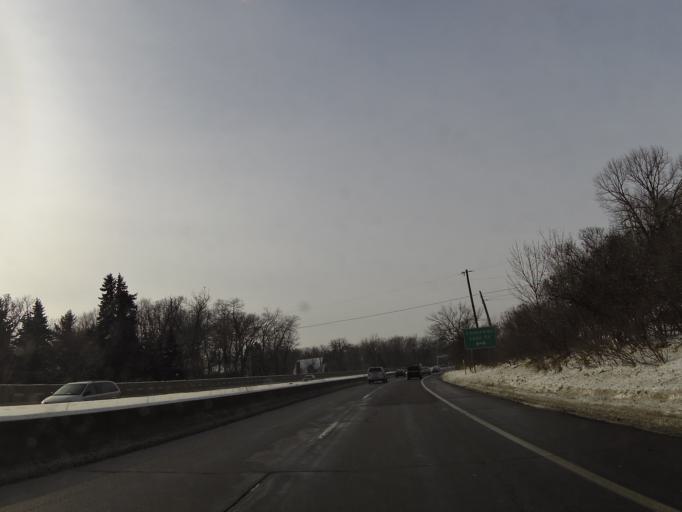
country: US
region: Minnesota
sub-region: Hennepin County
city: Excelsior
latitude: 44.9035
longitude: -93.5479
